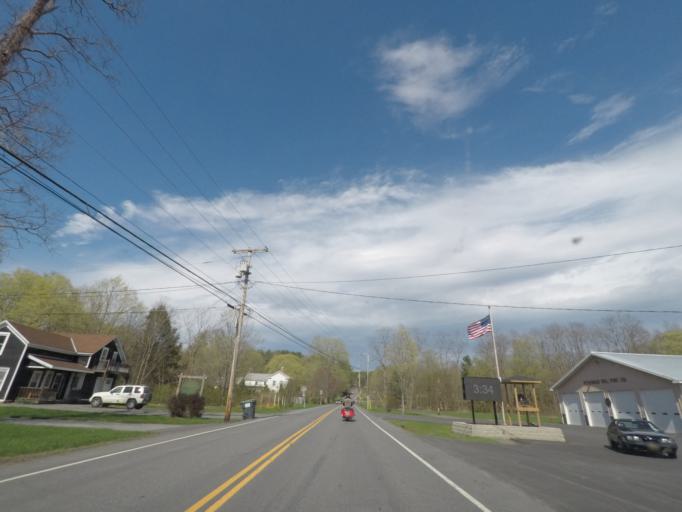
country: US
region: New York
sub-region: Greene County
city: Cairo
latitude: 42.3603
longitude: -74.0483
